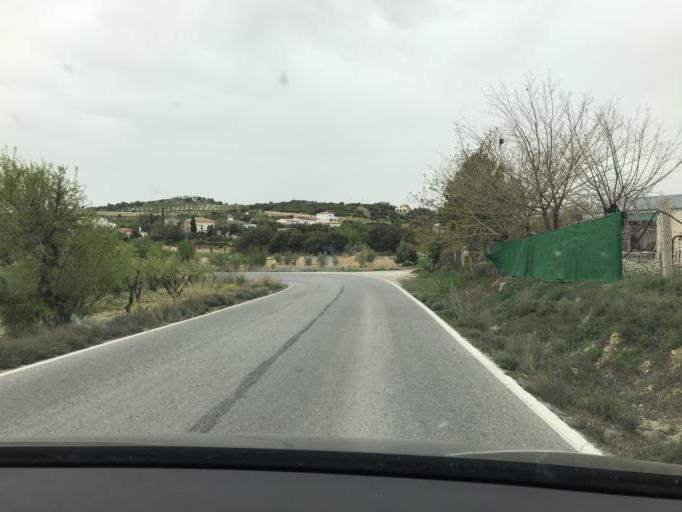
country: ES
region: Andalusia
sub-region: Provincia de Granada
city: Castril
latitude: 37.8134
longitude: -2.7655
